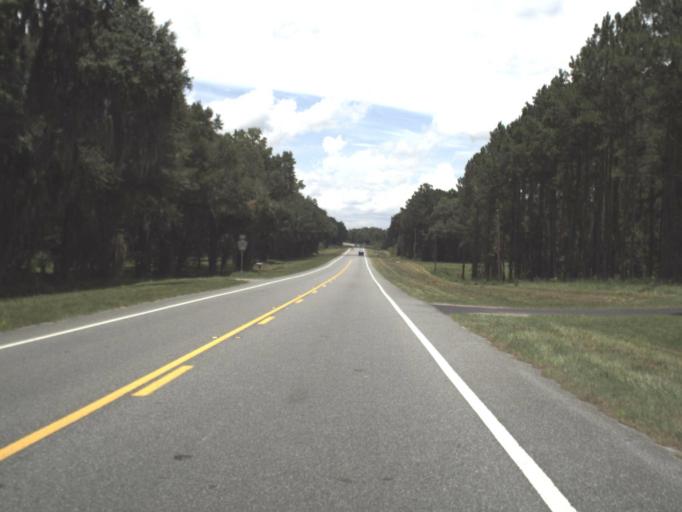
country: US
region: Florida
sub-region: Suwannee County
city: Live Oak
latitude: 30.3541
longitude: -82.9458
